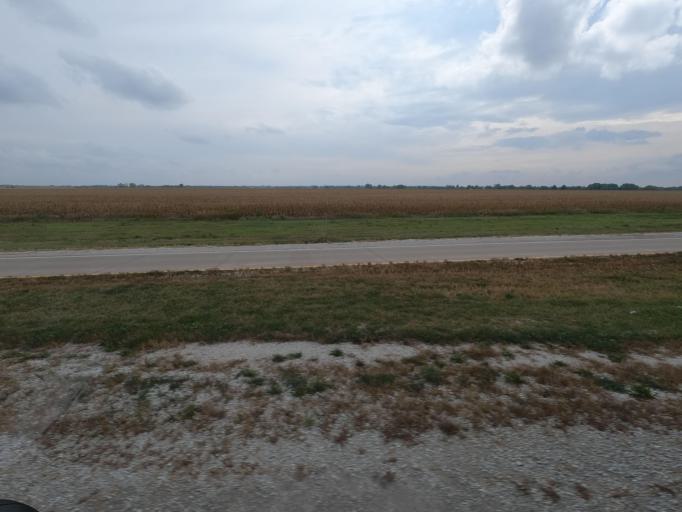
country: US
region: Iowa
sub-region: Wapello County
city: Ottumwa
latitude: 41.0901
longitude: -92.4052
